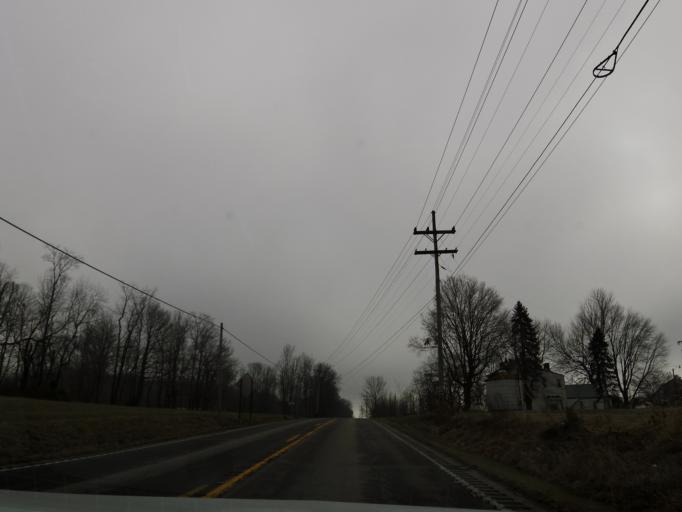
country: US
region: Indiana
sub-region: Jefferson County
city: North Madison
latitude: 38.8039
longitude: -85.4480
